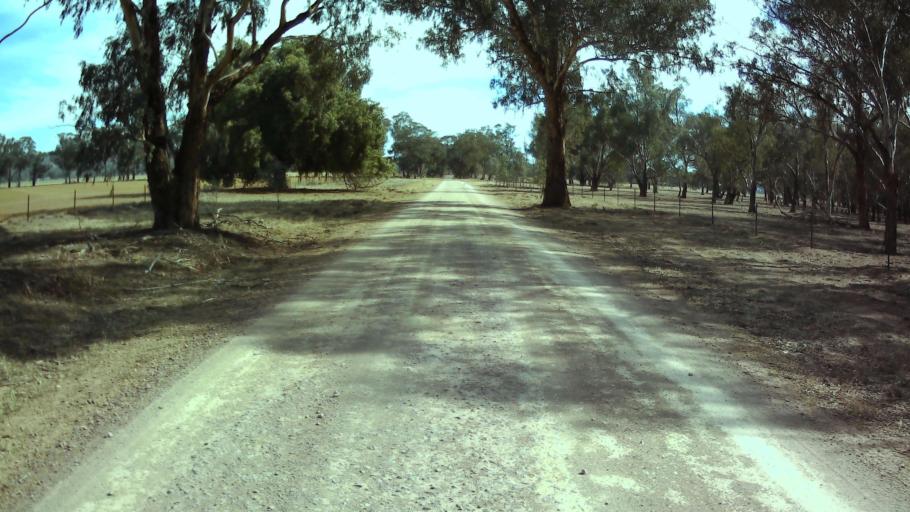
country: AU
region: New South Wales
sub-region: Weddin
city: Grenfell
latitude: -33.7021
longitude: 148.3020
